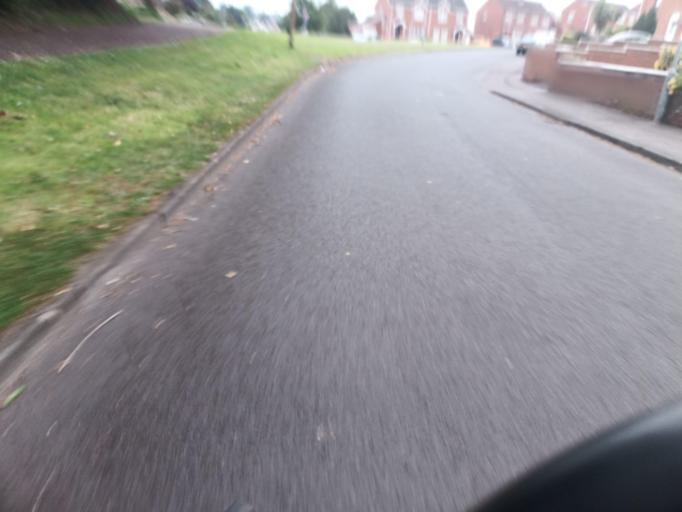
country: GB
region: Northern Ireland
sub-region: Ards District
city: Comber
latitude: 54.5526
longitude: -5.7335
